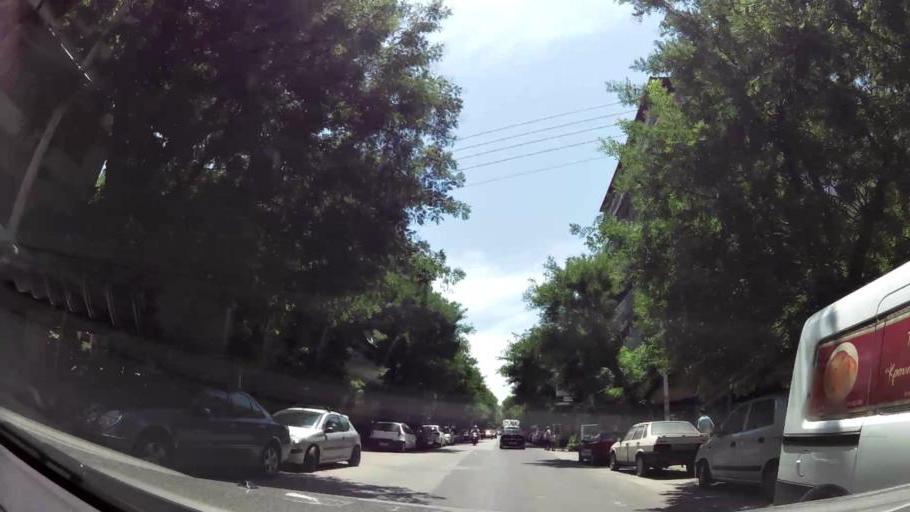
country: GR
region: Central Macedonia
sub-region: Nomos Thessalonikis
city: Triandria
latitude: 40.6098
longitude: 22.9575
